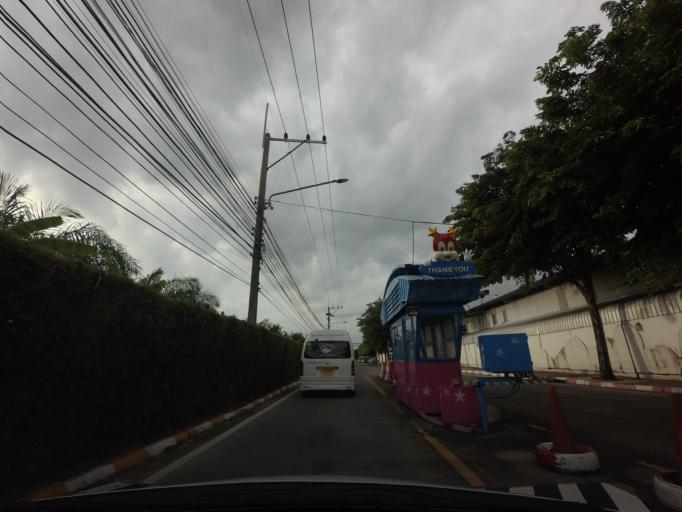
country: TH
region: Pathum Thani
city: Thanyaburi
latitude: 13.9916
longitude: 100.6745
